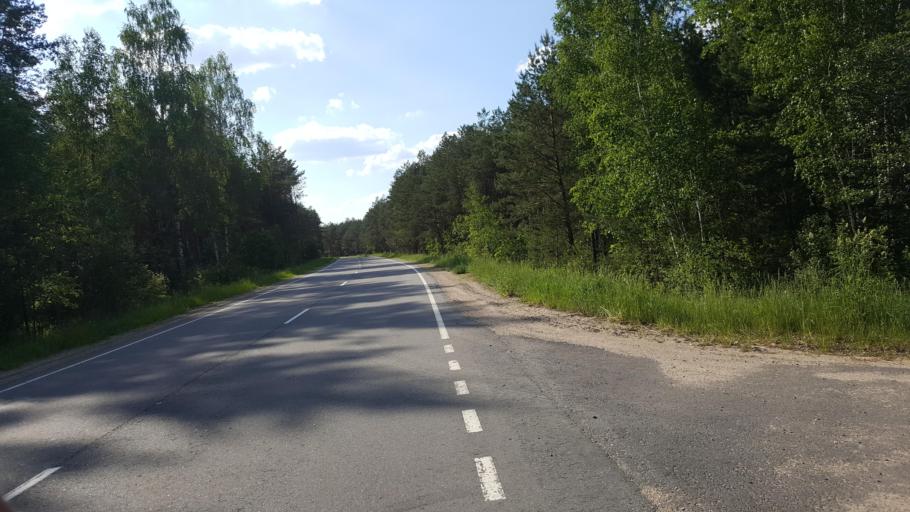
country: BY
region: Brest
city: Zhabinka
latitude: 52.3971
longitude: 24.0896
